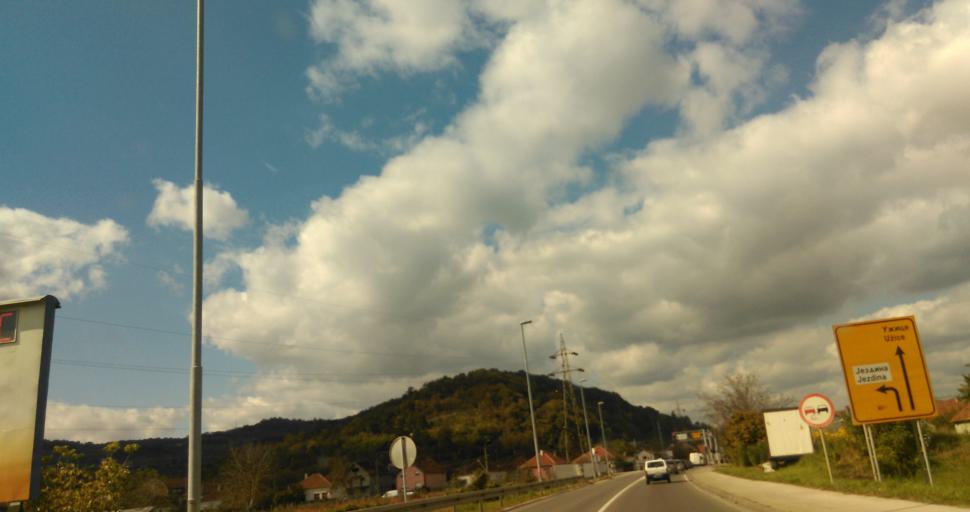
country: RS
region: Central Serbia
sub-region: Moravicki Okrug
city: Cacak
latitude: 43.8822
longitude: 20.3221
